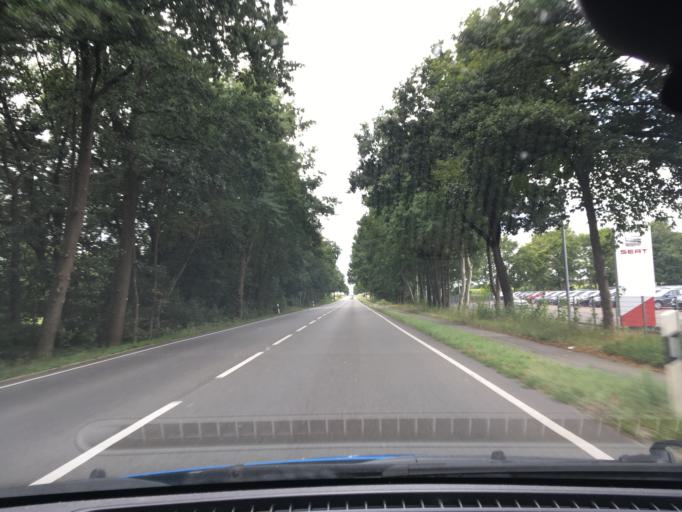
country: DE
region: Lower Saxony
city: Neu Wulmstorf
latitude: 53.4290
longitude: 9.7812
